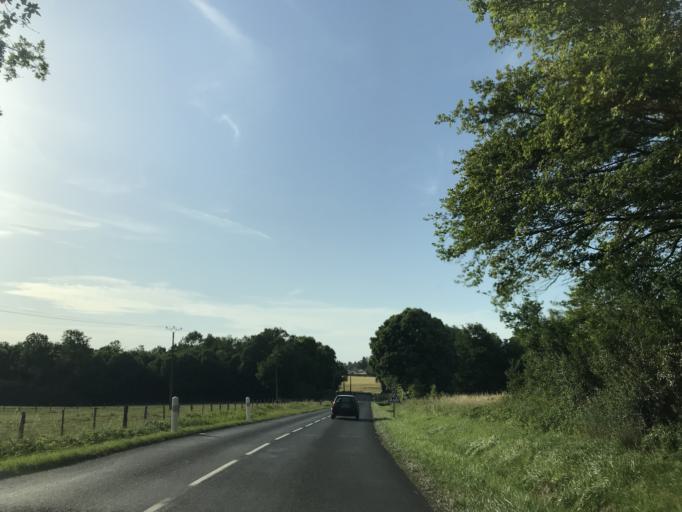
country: FR
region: Auvergne
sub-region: Departement du Puy-de-Dome
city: Lezoux
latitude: 45.8137
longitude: 3.3954
